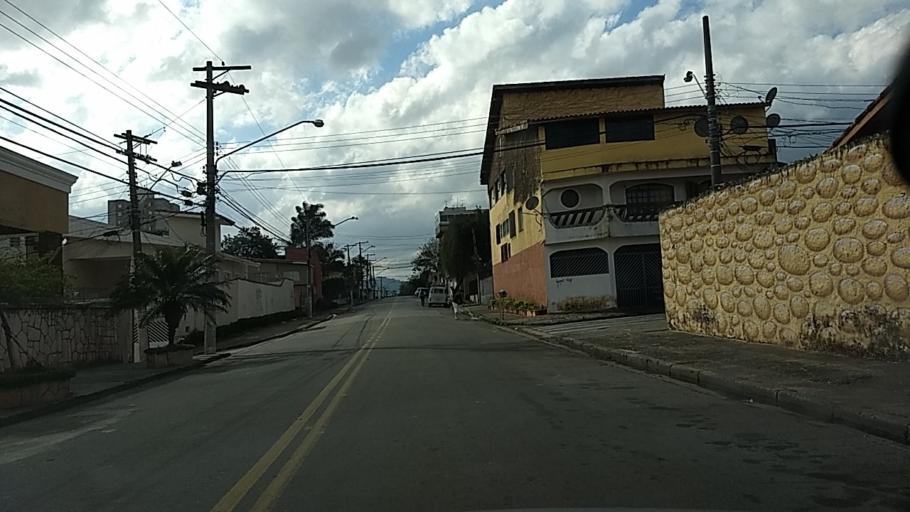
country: BR
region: Sao Paulo
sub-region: Carapicuiba
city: Carapicuiba
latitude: -23.5285
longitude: -46.8140
